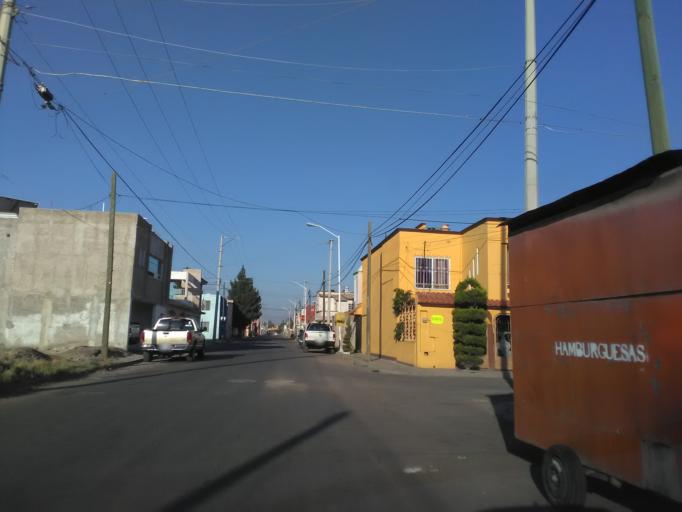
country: MX
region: Durango
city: Victoria de Durango
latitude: 24.0587
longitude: -104.6191
